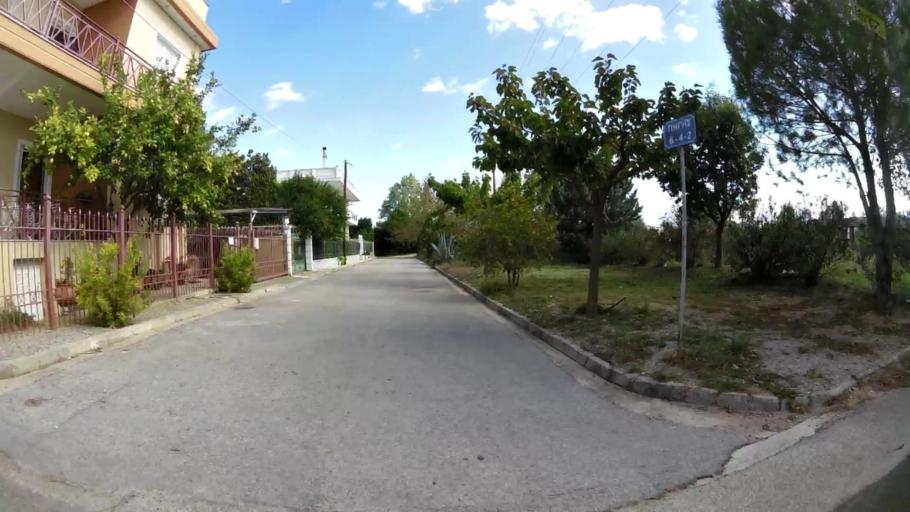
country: GR
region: Attica
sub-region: Nomarchia Anatolikis Attikis
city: Acharnes
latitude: 38.1015
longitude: 23.7389
